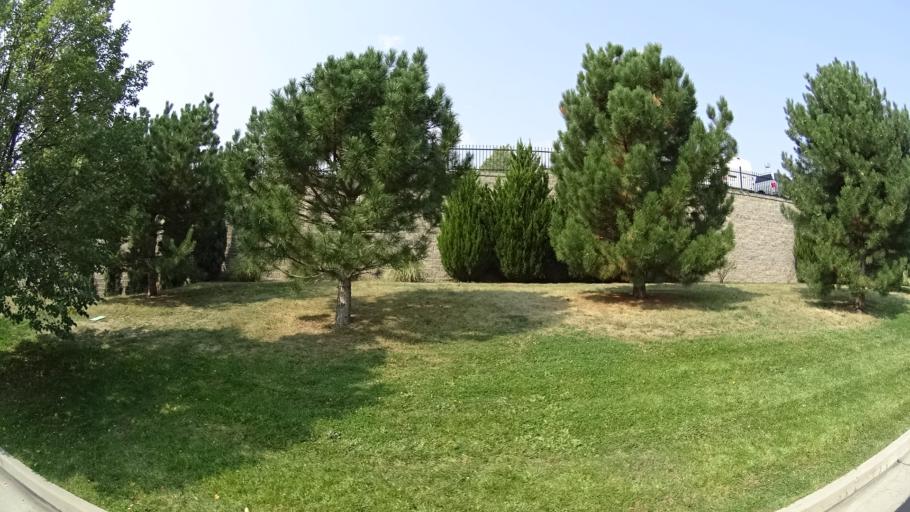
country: US
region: Colorado
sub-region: El Paso County
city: Stratmoor
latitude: 38.8123
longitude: -104.7553
